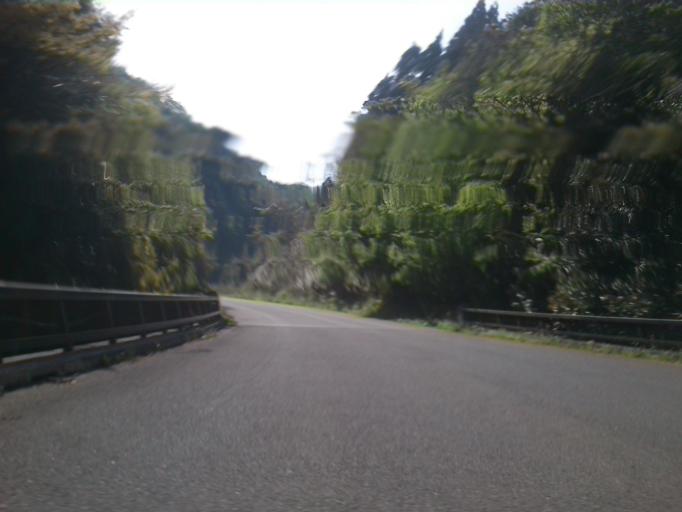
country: JP
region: Kyoto
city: Miyazu
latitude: 35.6342
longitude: 135.2099
